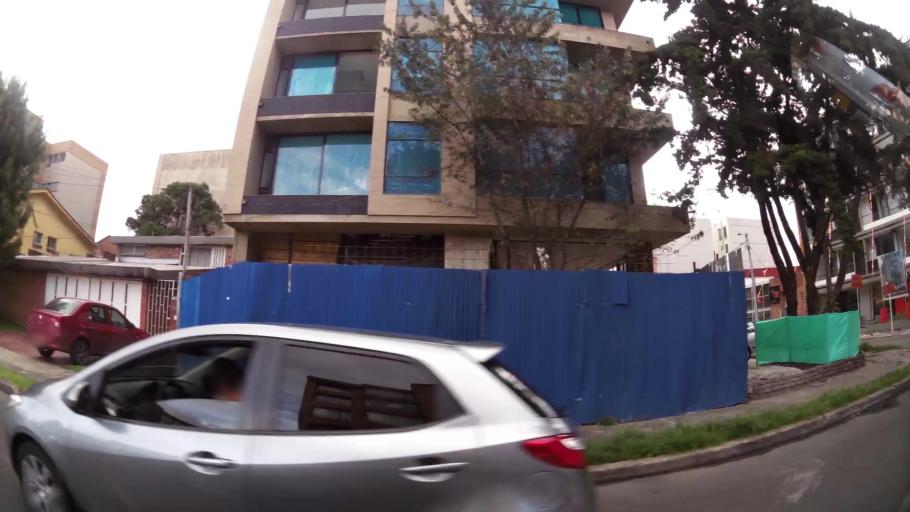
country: CO
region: Bogota D.C.
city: Barrio San Luis
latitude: 4.6932
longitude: -74.0484
